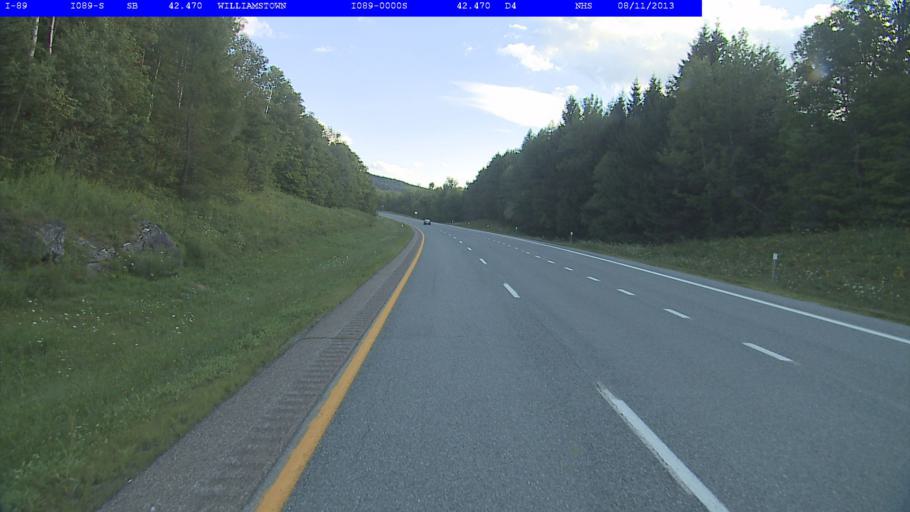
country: US
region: Vermont
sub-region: Washington County
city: Northfield
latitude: 44.1088
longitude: -72.6121
